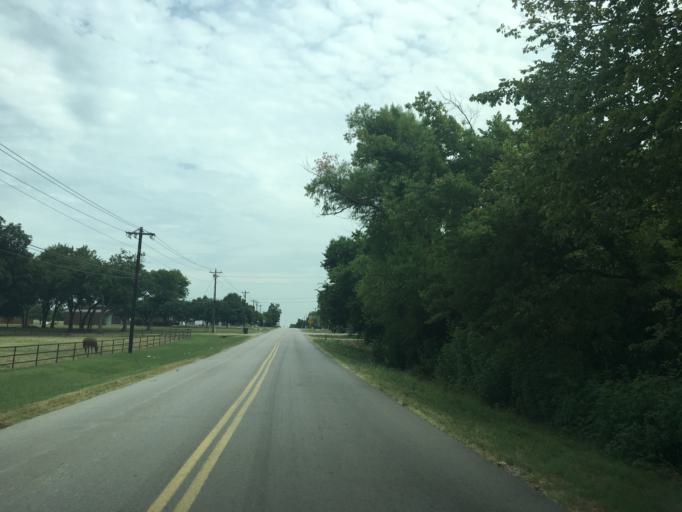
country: US
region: Texas
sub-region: Collin County
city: Wylie
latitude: 32.9964
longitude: -96.5217
